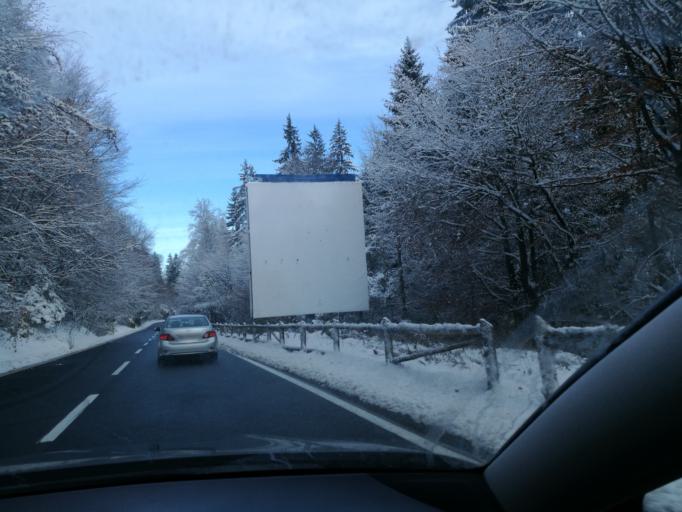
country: RO
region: Brasov
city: Brasov
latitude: 45.6265
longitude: 25.5501
